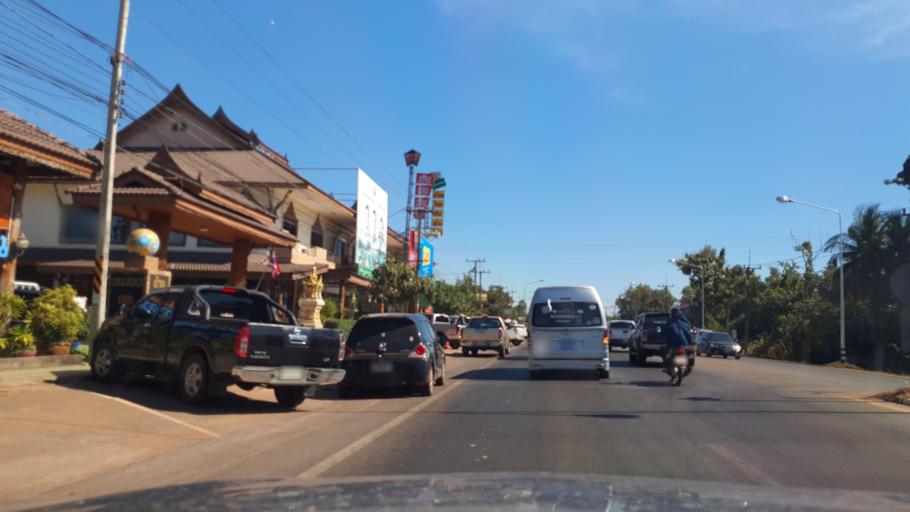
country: TH
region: Sakon Nakhon
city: Tao Ngoi
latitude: 17.0822
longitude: 104.1924
